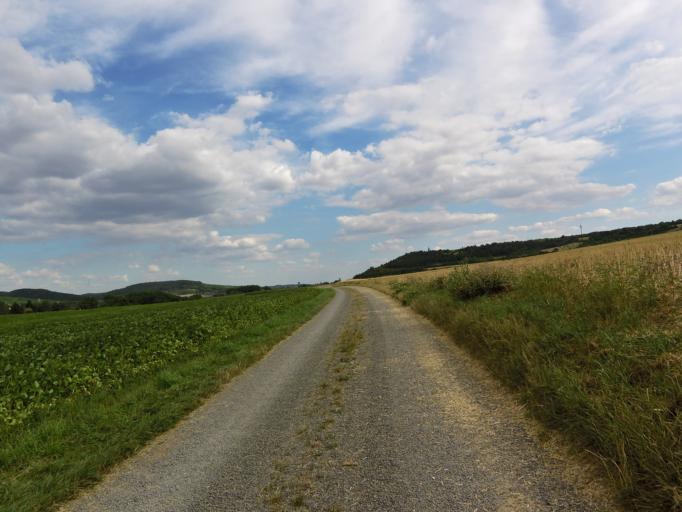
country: DE
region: Bavaria
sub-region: Regierungsbezirk Unterfranken
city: Randersacker
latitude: 49.7512
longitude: 9.9731
